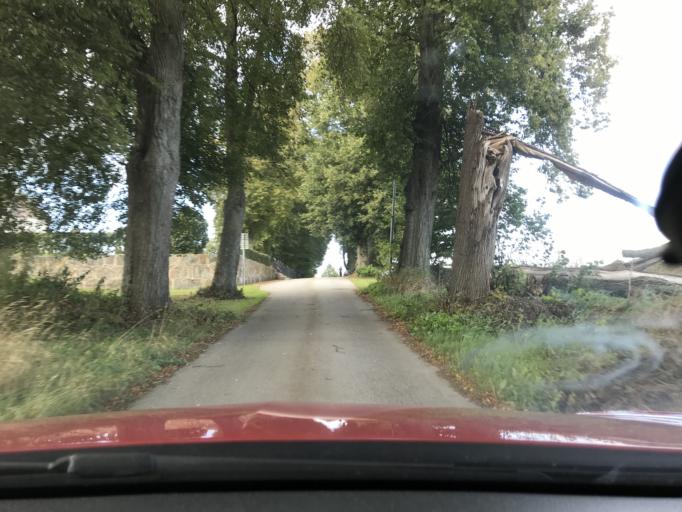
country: SE
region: Skane
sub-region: Simrishamns Kommun
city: Kivik
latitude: 55.7132
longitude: 14.1514
